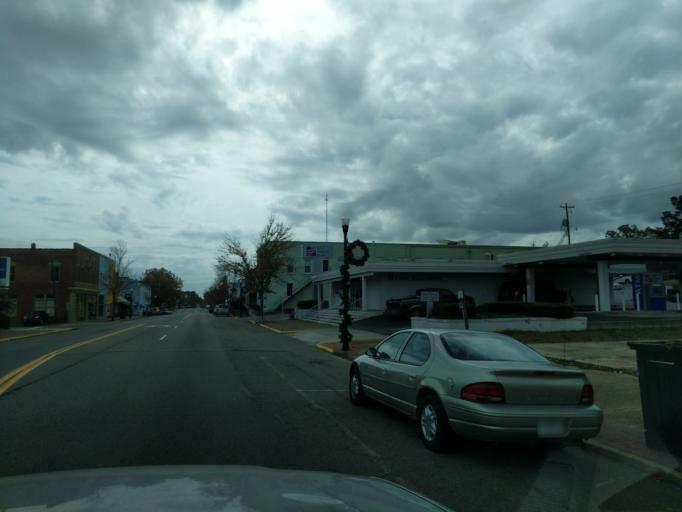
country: US
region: South Carolina
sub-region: Saluda County
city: Saluda
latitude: 34.0041
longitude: -81.7724
